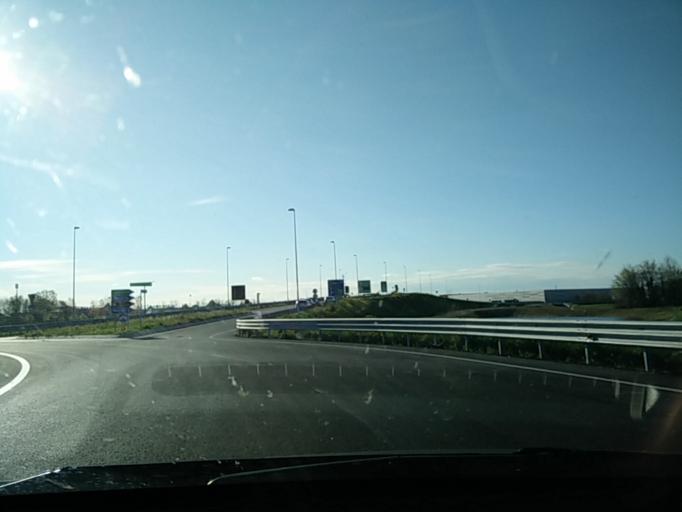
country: IT
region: Veneto
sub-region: Provincia di Venezia
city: Marcon-Gaggio-Colmello
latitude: 45.5488
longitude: 12.2962
